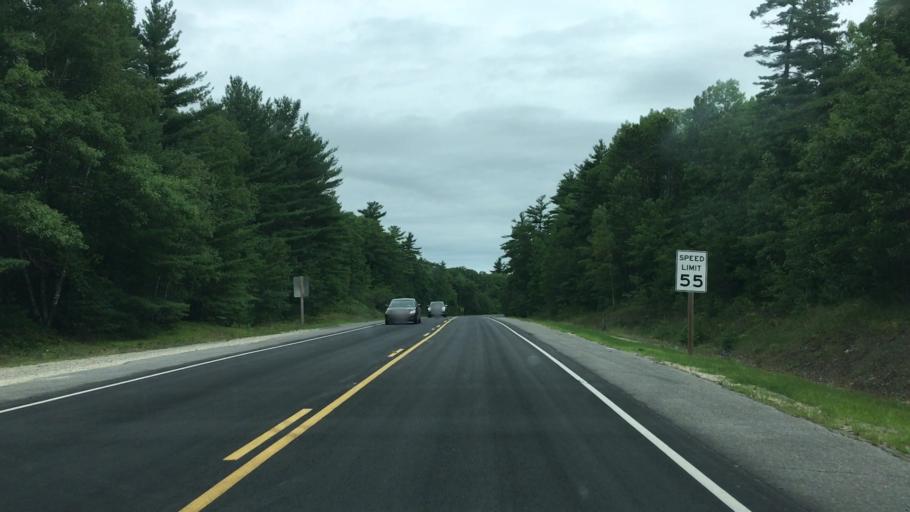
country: US
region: Maine
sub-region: Washington County
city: Cherryfield
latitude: 44.9045
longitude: -67.8565
